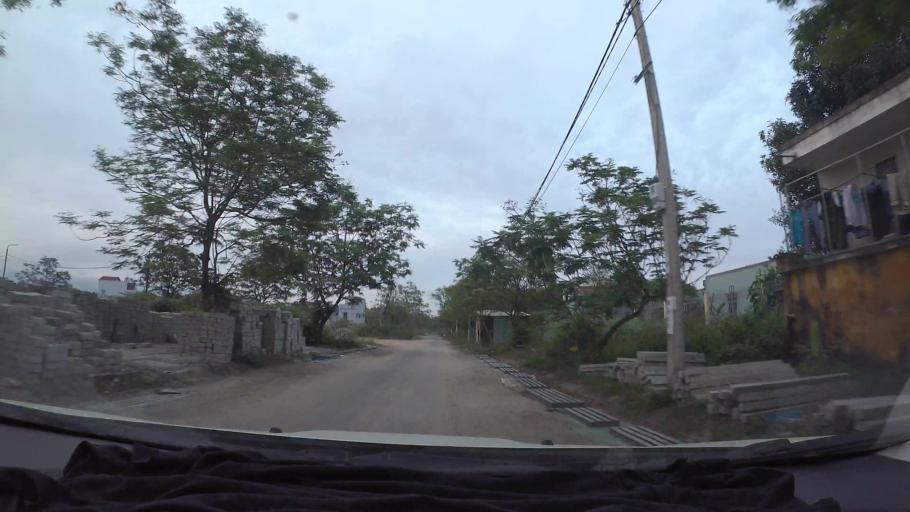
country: VN
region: Da Nang
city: Lien Chieu
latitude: 16.0709
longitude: 108.1079
